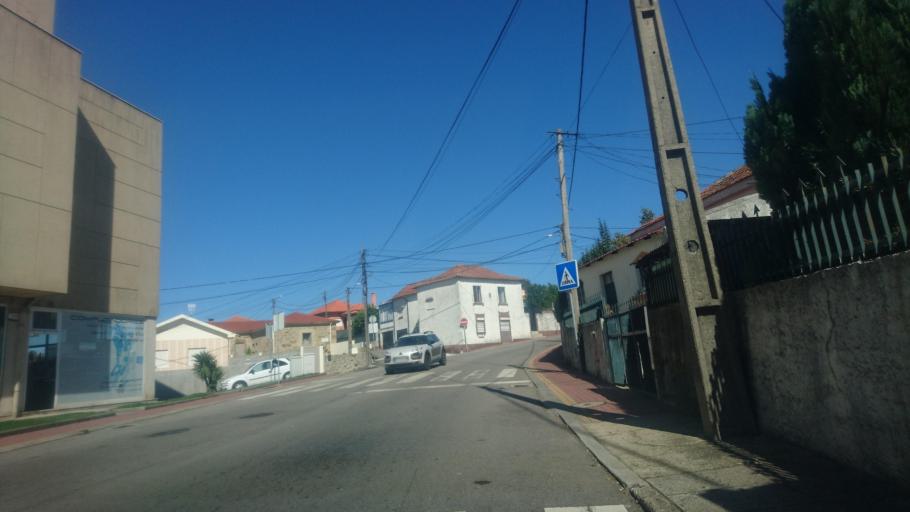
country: PT
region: Aveiro
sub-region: Santa Maria da Feira
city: Lamas
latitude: 40.9807
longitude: -8.5761
